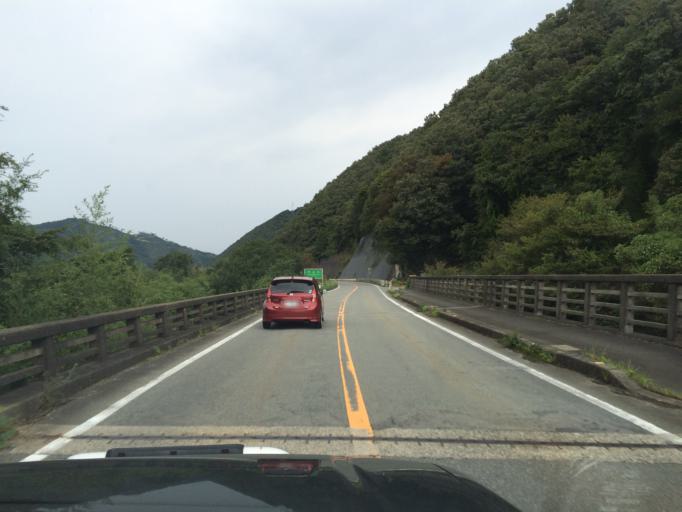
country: JP
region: Hyogo
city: Toyooka
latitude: 35.3609
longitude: 134.8283
